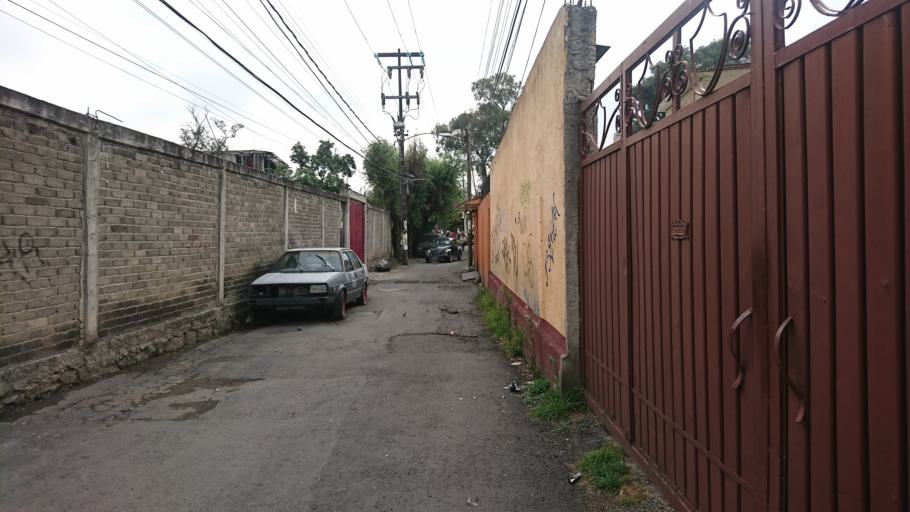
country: MX
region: Mexico City
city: Iztapalapa
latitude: 19.3254
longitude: -99.1037
